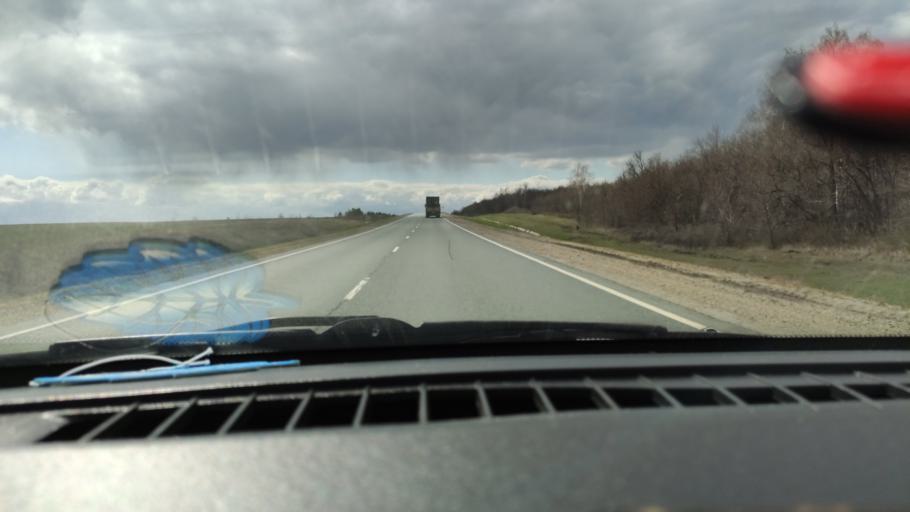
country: RU
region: Saratov
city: Alekseyevka
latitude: 52.2370
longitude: 47.9049
